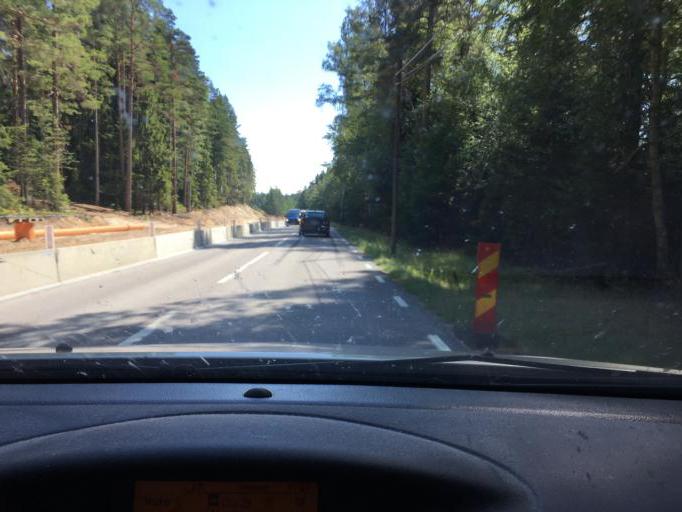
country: SE
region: Stockholm
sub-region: Varmdo Kommun
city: Mortnas
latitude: 59.2763
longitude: 18.4548
